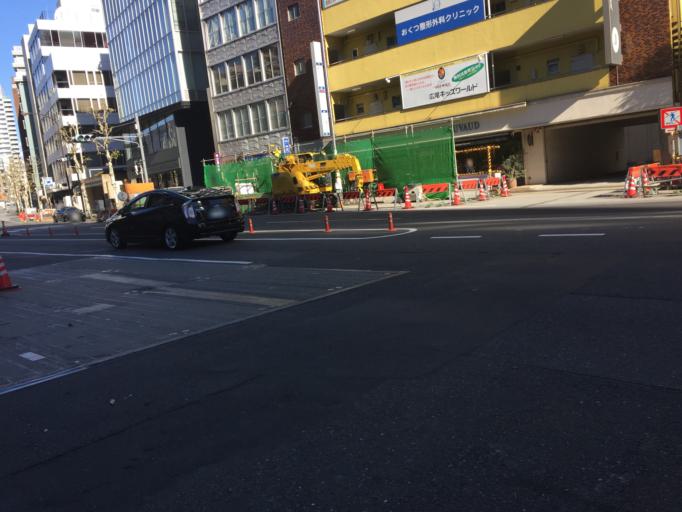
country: JP
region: Tokyo
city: Tokyo
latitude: 35.6522
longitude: 139.7221
